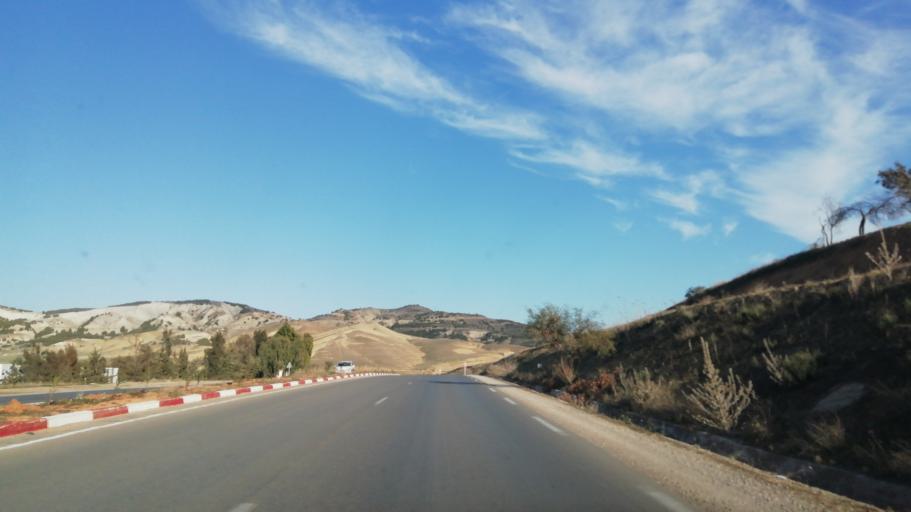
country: DZ
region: Mascara
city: Bou Hanifia el Hamamat
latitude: 35.3367
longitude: -0.0400
